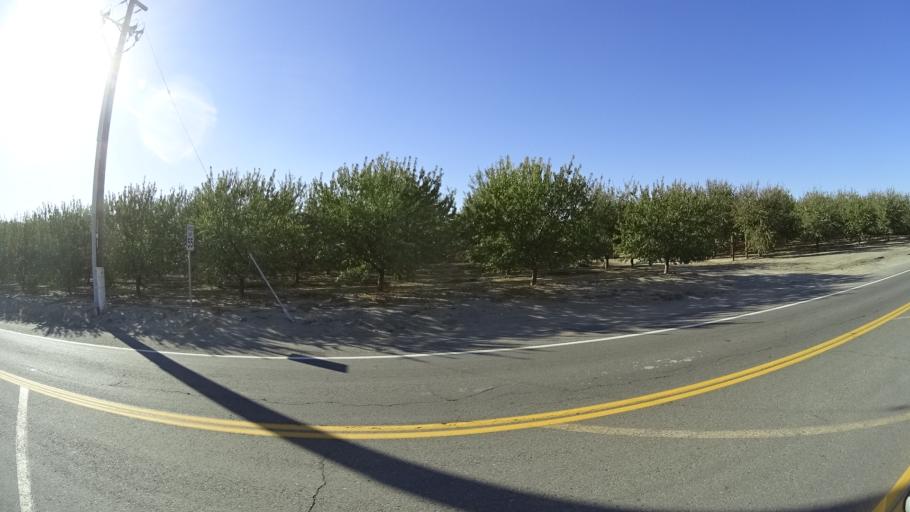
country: US
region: California
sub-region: Kern County
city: Greenacres
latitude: 35.2808
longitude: -119.1098
